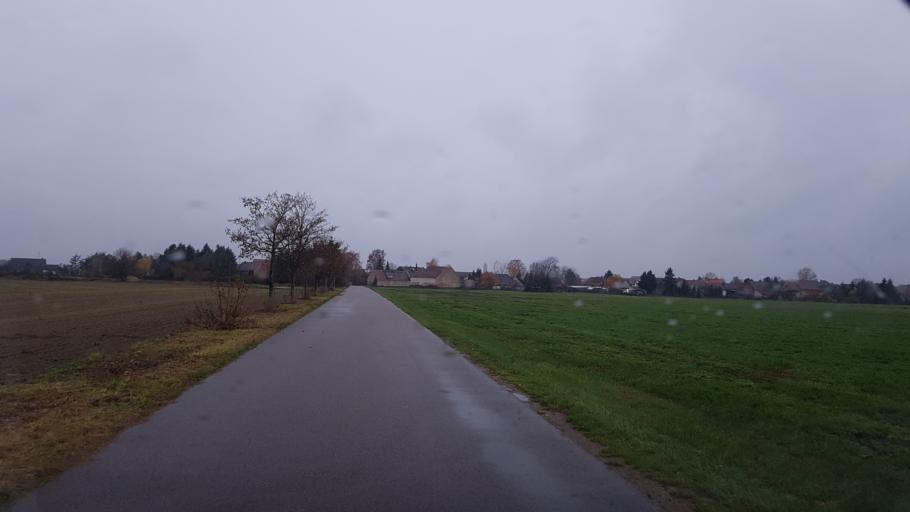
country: DE
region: Brandenburg
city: Herzberg
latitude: 51.6513
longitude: 13.2271
